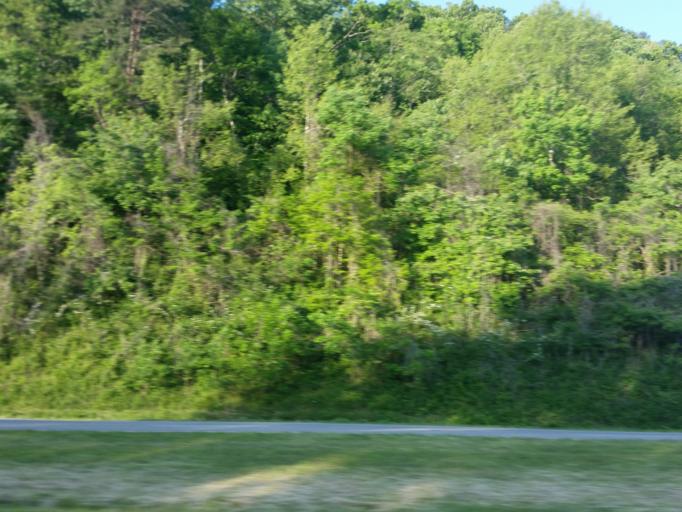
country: US
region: Virginia
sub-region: Washington County
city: Abingdon
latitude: 36.7765
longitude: -82.0809
